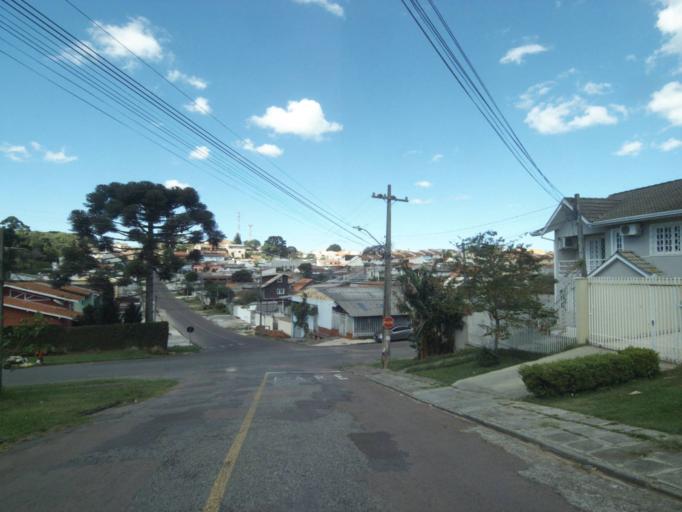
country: BR
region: Parana
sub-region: Curitiba
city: Curitiba
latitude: -25.3755
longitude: -49.2502
